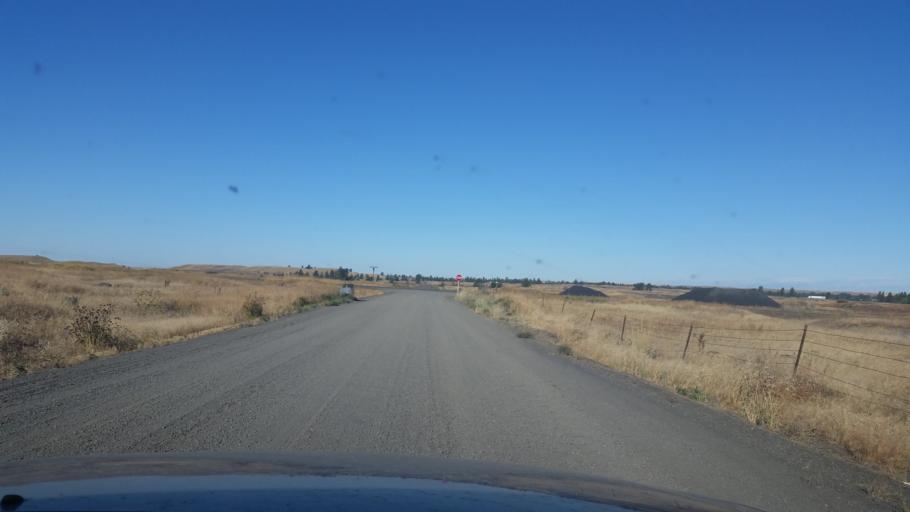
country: US
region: Washington
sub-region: Spokane County
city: Medical Lake
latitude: 47.3840
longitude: -117.8418
